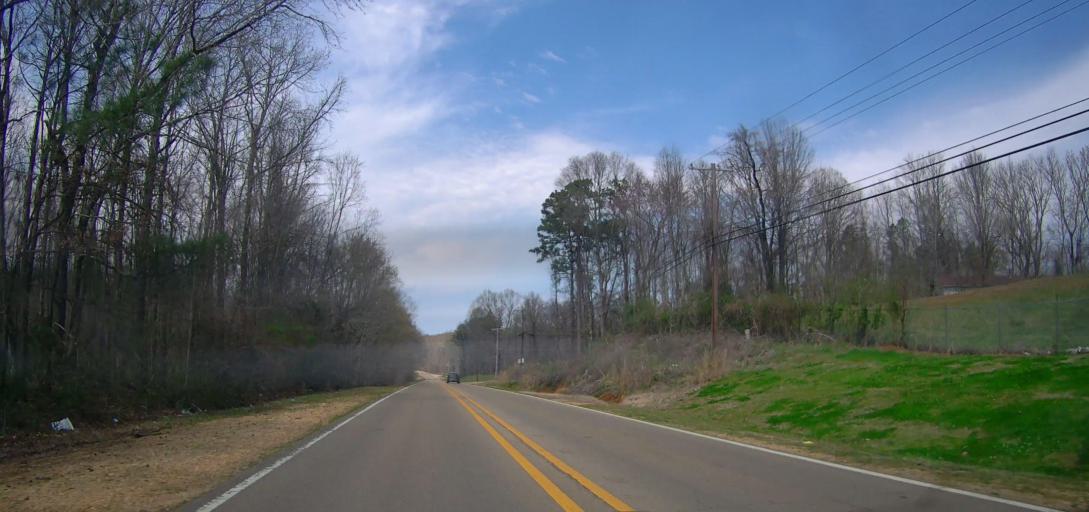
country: US
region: Mississippi
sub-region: Union County
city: New Albany
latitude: 34.4614
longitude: -88.9795
